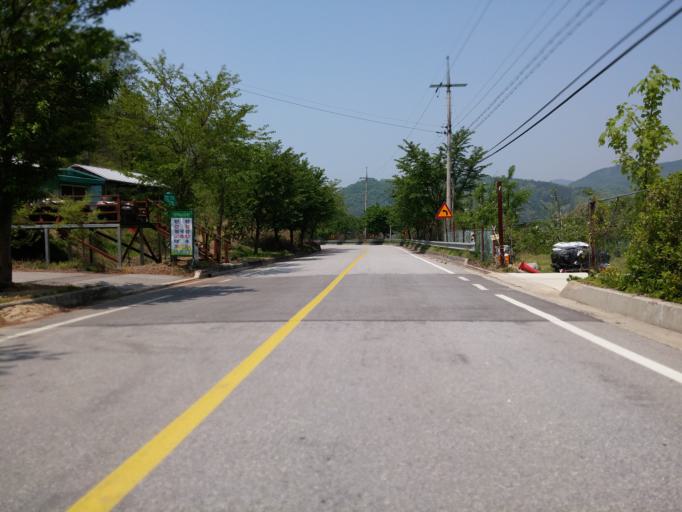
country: KR
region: Chungcheongbuk-do
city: Okcheon
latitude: 36.4311
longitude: 127.5763
